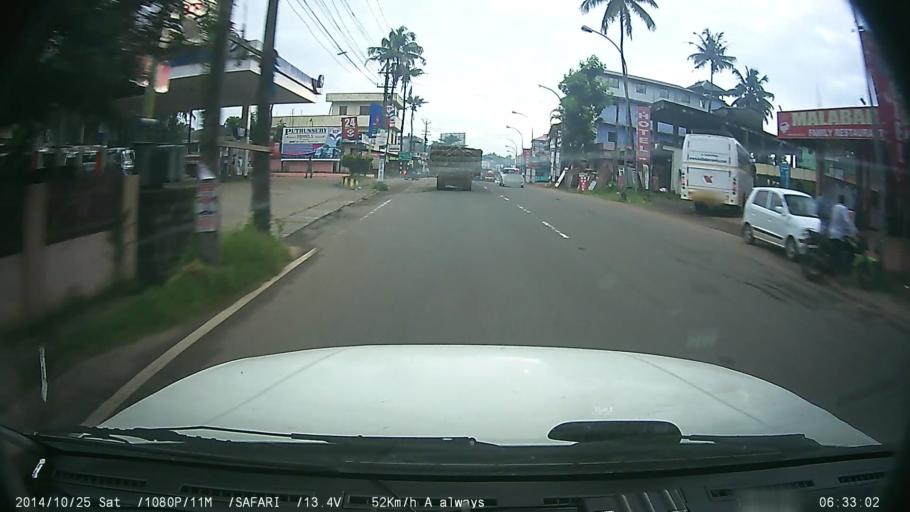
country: IN
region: Kerala
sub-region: Ernakulam
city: Muvattupula
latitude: 10.0197
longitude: 76.5619
